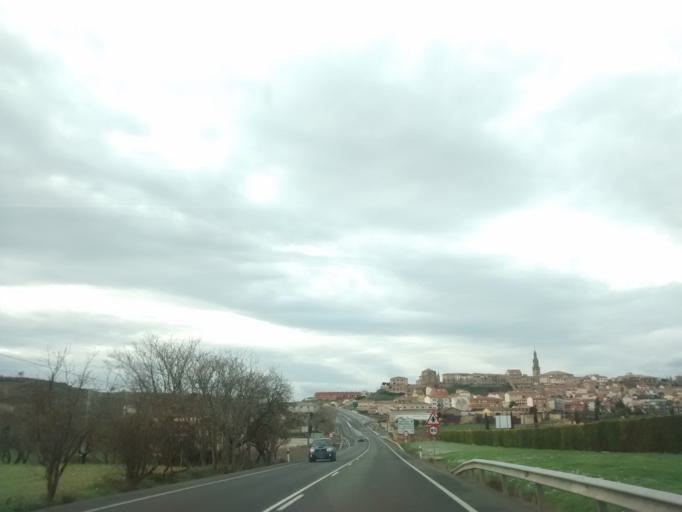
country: ES
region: La Rioja
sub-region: Provincia de La Rioja
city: Briones
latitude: 42.5384
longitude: -2.7775
